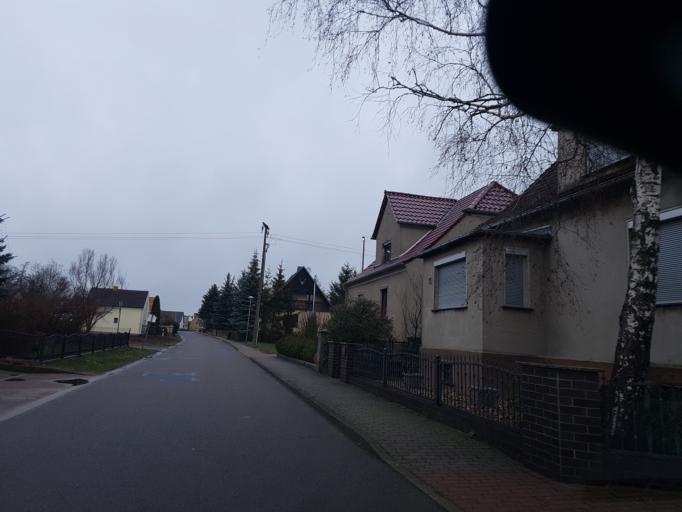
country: DE
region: Brandenburg
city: Muhlberg
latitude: 51.4673
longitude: 13.2981
